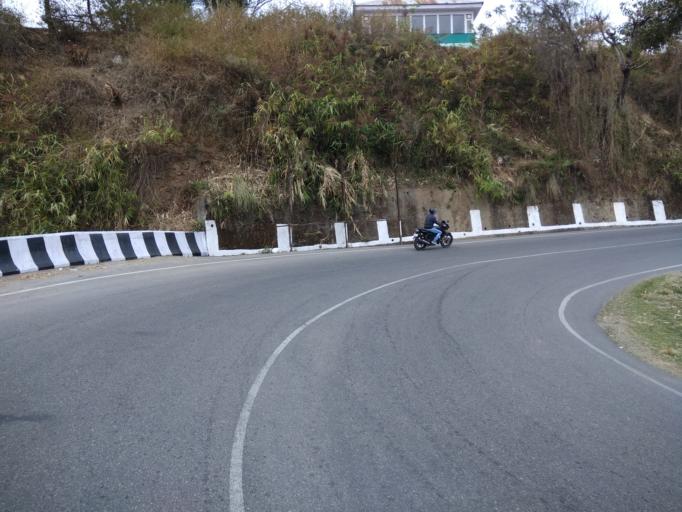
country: IN
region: Himachal Pradesh
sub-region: Kangra
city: Dharmsala
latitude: 32.2032
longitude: 76.3259
